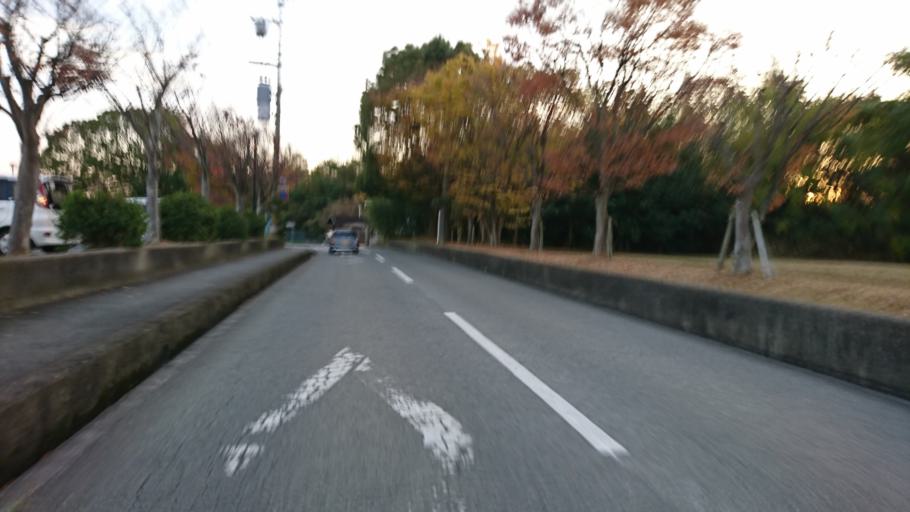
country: JP
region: Hyogo
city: Kakogawacho-honmachi
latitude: 34.7735
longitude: 134.8643
